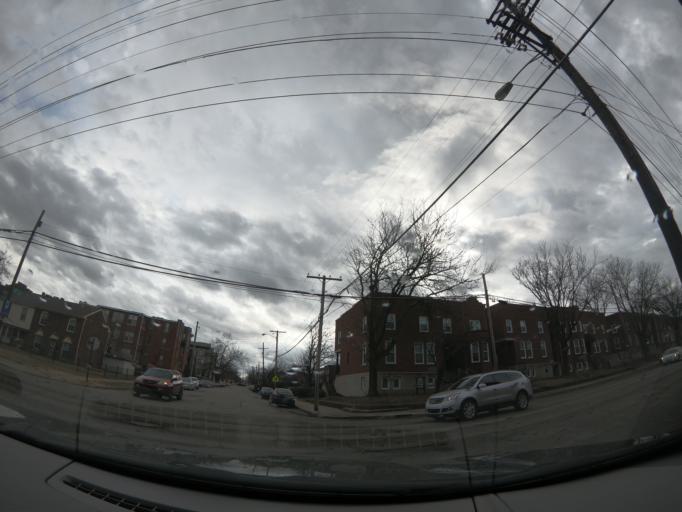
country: US
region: Kentucky
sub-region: Jefferson County
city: Louisville
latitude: 38.2263
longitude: -85.7636
